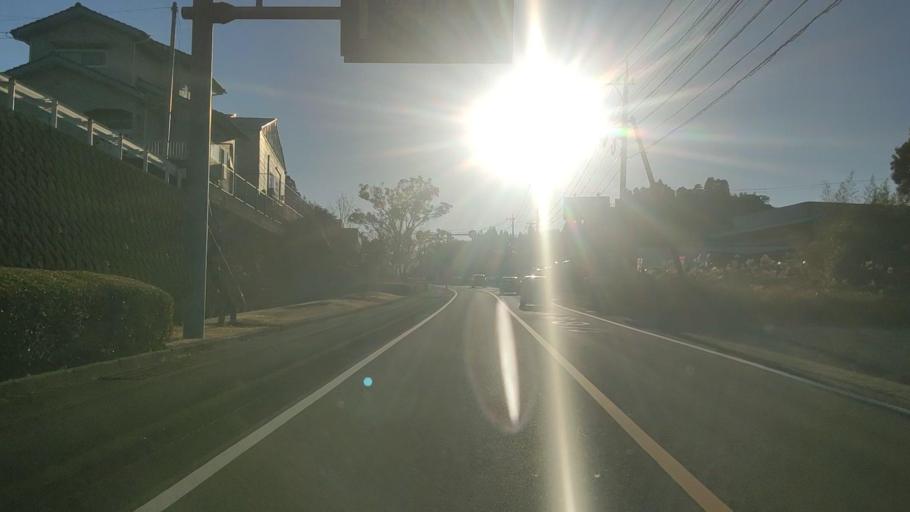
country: JP
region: Miyazaki
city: Miyazaki-shi
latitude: 31.8666
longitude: 131.3906
